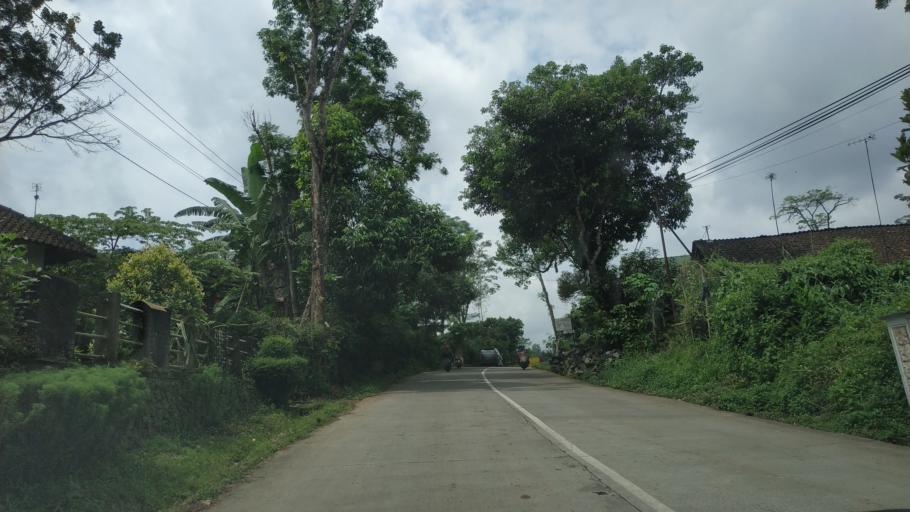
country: ID
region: Central Java
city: Weleri
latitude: -7.0990
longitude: 110.0638
